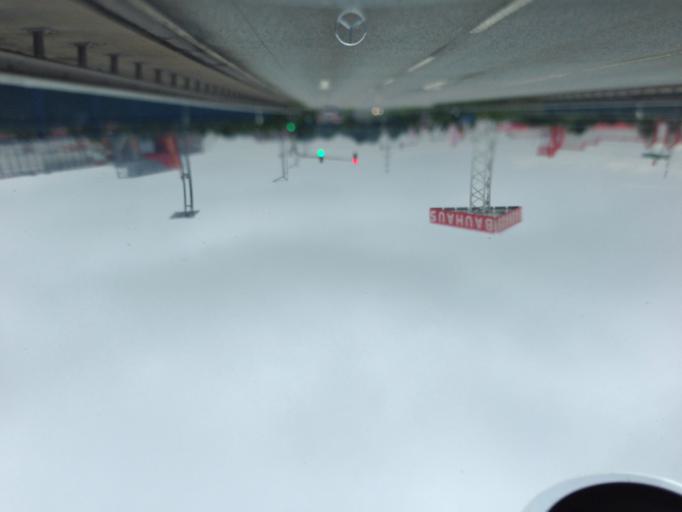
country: DE
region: Schleswig-Holstein
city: Stapelfeld
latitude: 53.5751
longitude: 10.1990
